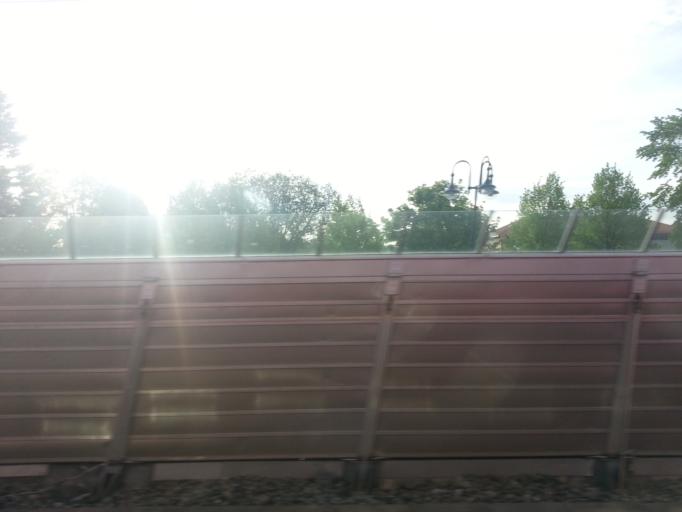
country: NO
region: Akershus
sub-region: Ullensaker
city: Klofta
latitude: 60.0750
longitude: 11.1398
